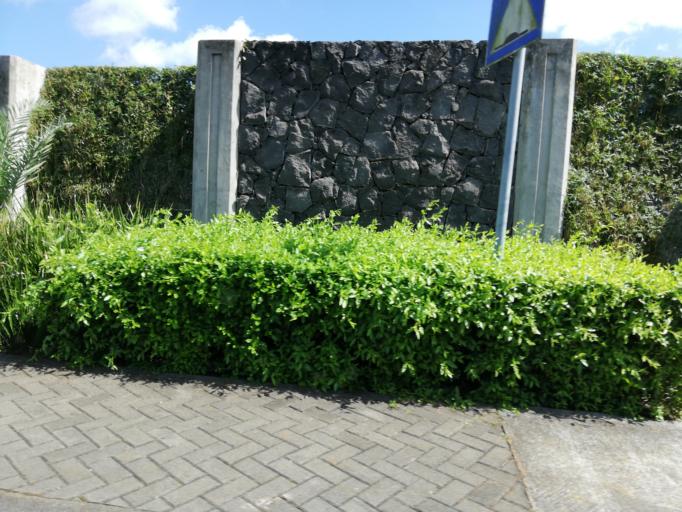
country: MU
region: Moka
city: Moka
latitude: -20.2234
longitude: 57.4947
